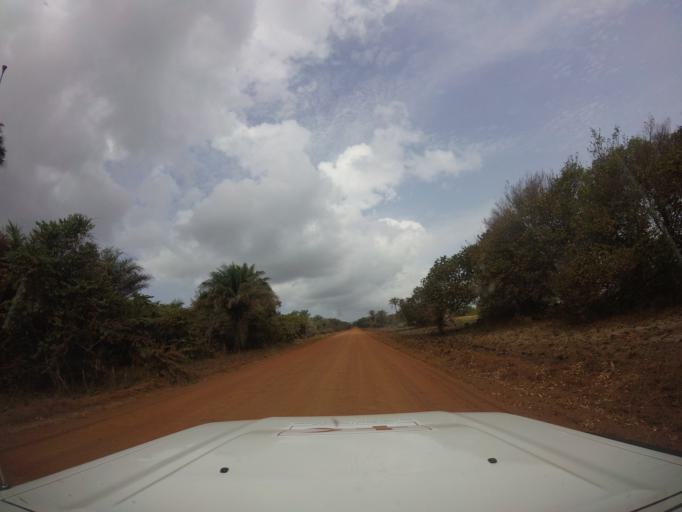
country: LR
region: Grand Cape Mount
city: Robertsport
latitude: 6.6887
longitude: -11.2557
